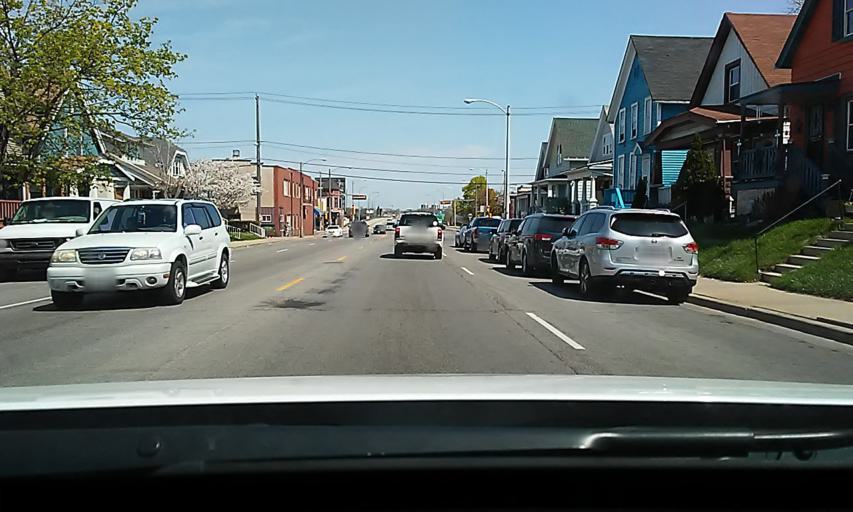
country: US
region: Wisconsin
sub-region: Milwaukee County
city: West Milwaukee
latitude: 43.0204
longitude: -87.9576
